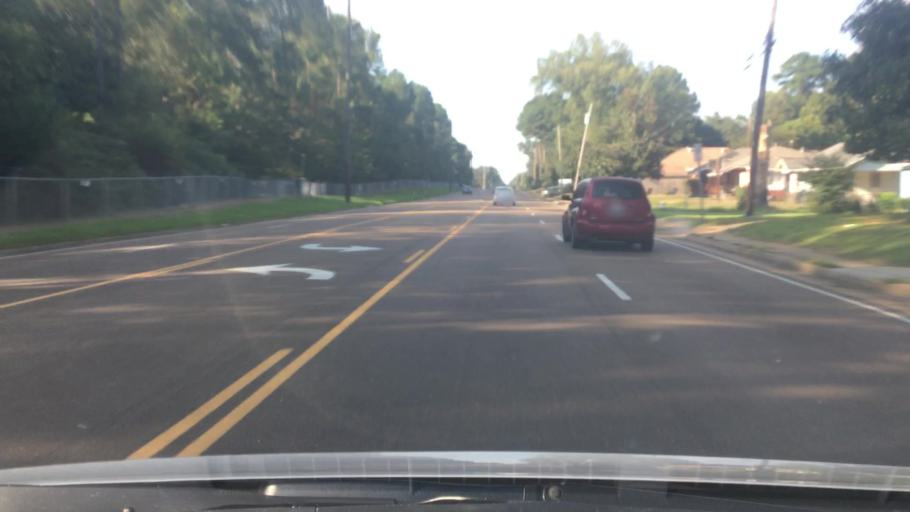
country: US
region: Mississippi
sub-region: Hinds County
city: Jackson
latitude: 32.3643
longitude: -90.1927
